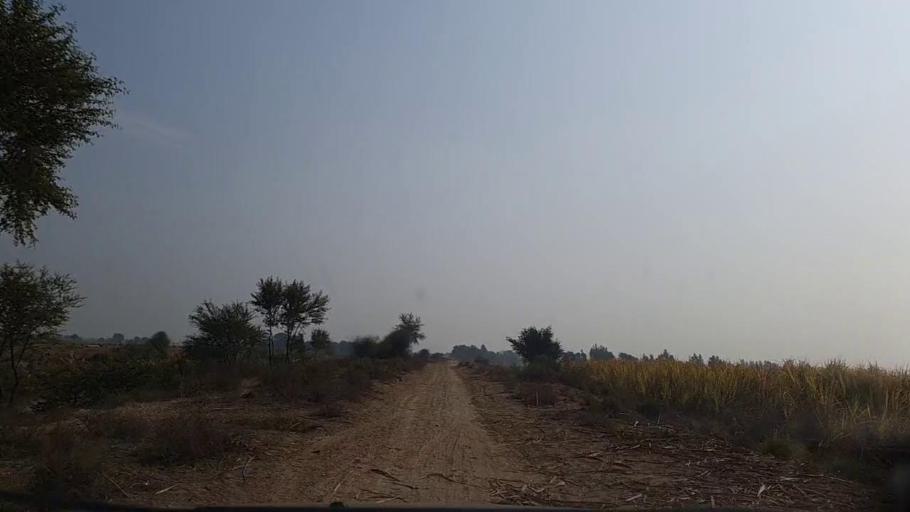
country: PK
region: Sindh
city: Sanghar
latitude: 26.0427
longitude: 68.9926
